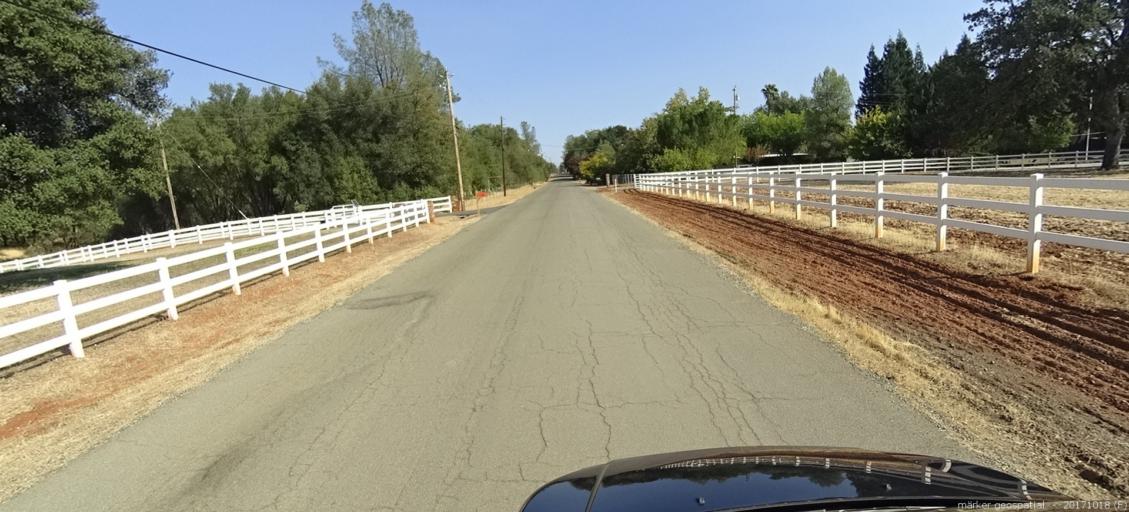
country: US
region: California
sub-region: Shasta County
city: Palo Cedro
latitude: 40.5529
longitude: -122.2820
